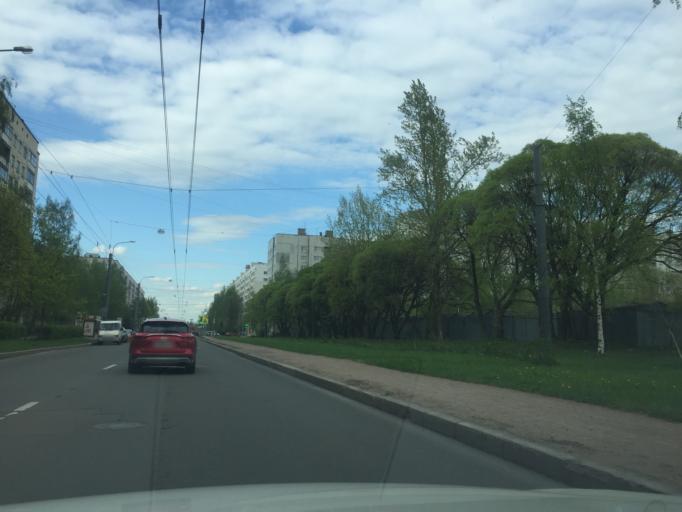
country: RU
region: Leningrad
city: Parnas
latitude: 60.0543
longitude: 30.3442
